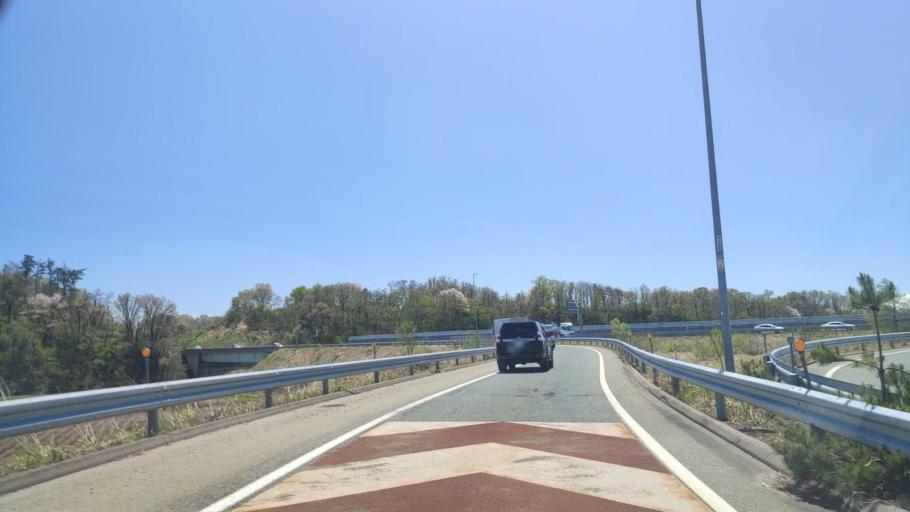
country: JP
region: Yamagata
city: Shinjo
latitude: 38.7387
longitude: 140.3003
